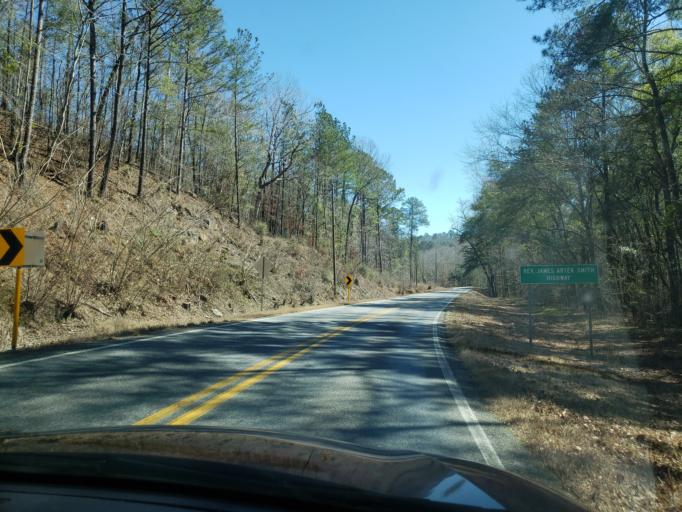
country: US
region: Alabama
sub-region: Elmore County
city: Eclectic
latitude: 32.6768
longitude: -85.9069
